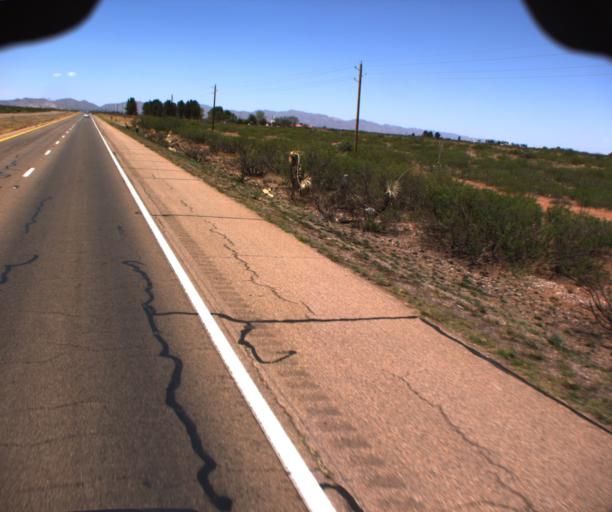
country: US
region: Arizona
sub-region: Cochise County
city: Pirtleville
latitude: 31.3561
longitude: -109.6199
